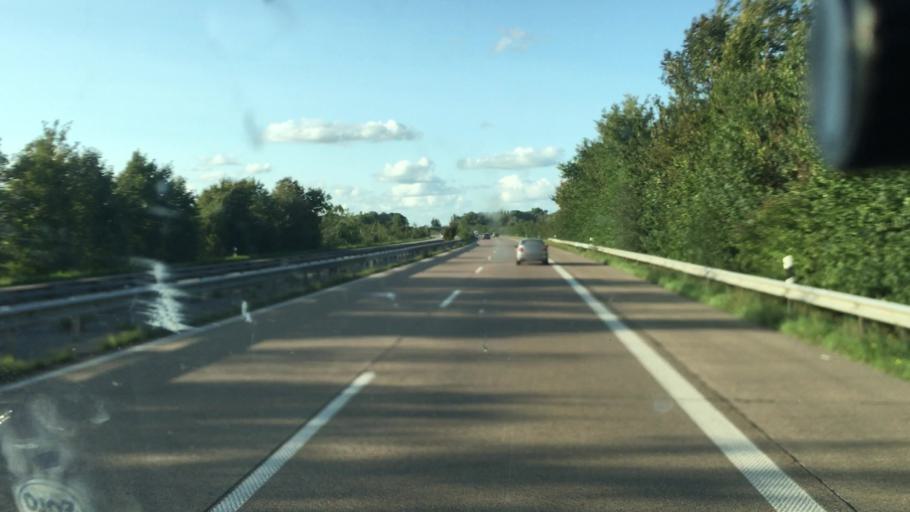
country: DE
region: Lower Saxony
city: Sande
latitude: 53.4676
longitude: 8.0172
